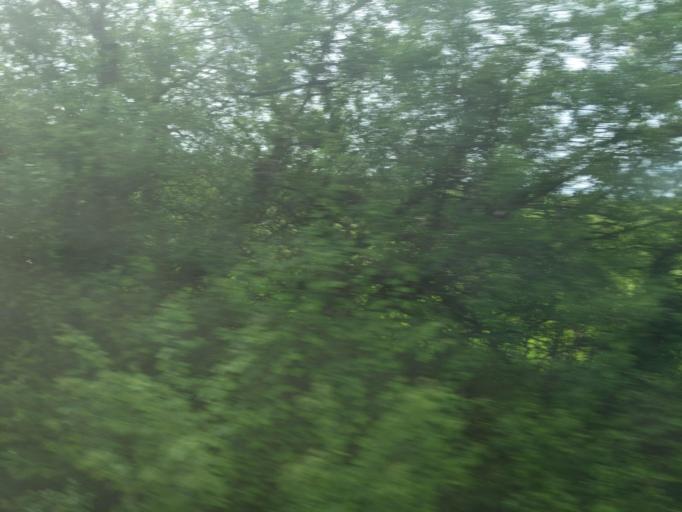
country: GB
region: England
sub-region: Devon
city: Winkleigh
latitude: 50.9582
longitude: -3.9451
